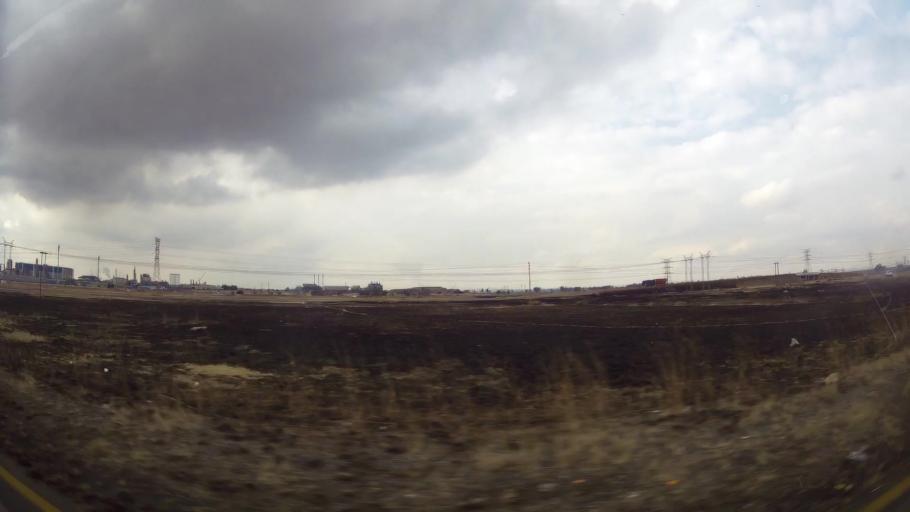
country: ZA
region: Orange Free State
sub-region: Fezile Dabi District Municipality
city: Sasolburg
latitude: -26.8399
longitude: 27.8717
